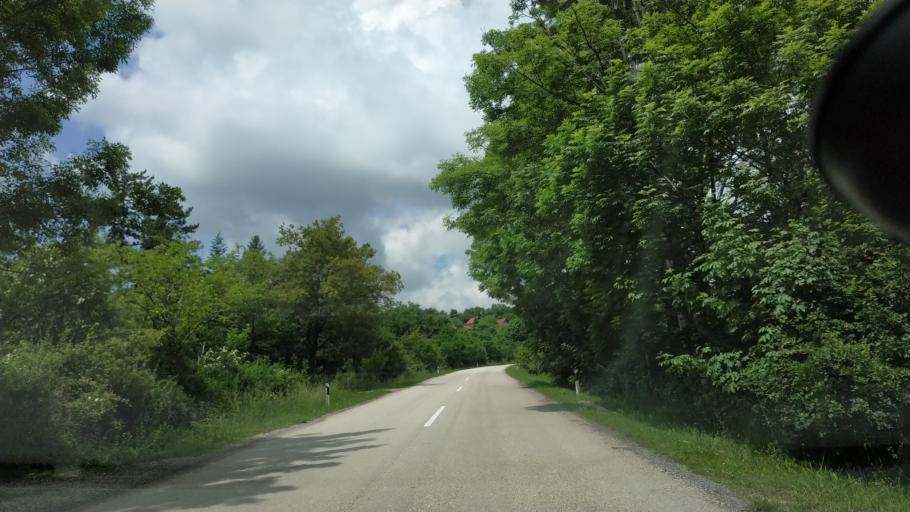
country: RS
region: Central Serbia
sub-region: Borski Okrug
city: Bor
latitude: 44.0833
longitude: 22.0119
